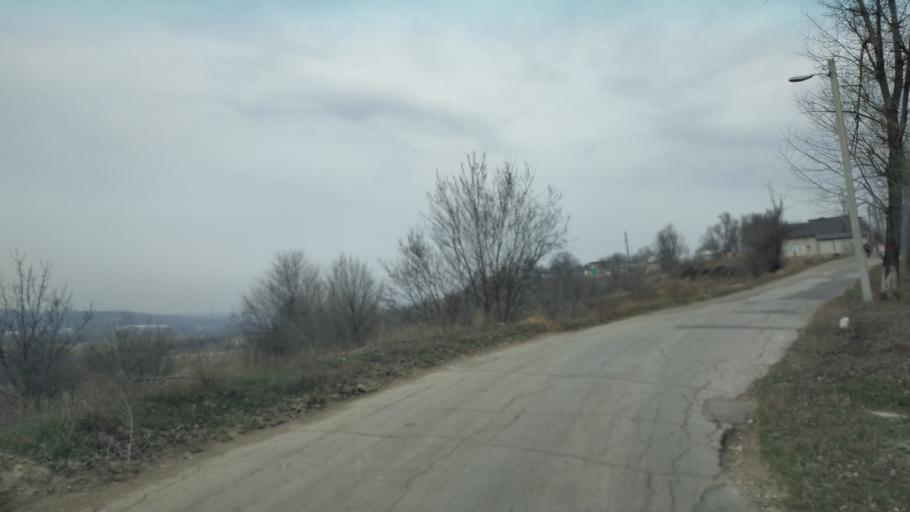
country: MD
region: Chisinau
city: Singera
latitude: 46.9334
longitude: 28.9787
